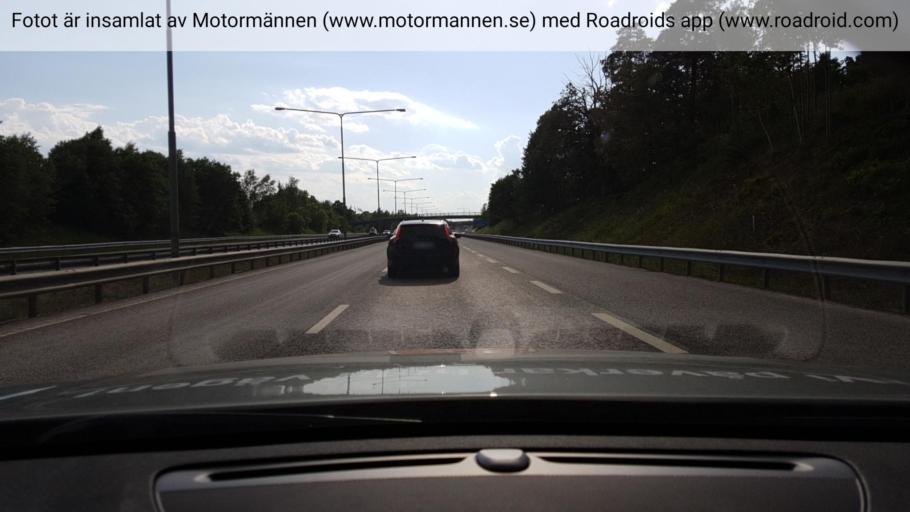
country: SE
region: Stockholm
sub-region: Nacka Kommun
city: Boo
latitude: 59.3168
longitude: 18.2668
